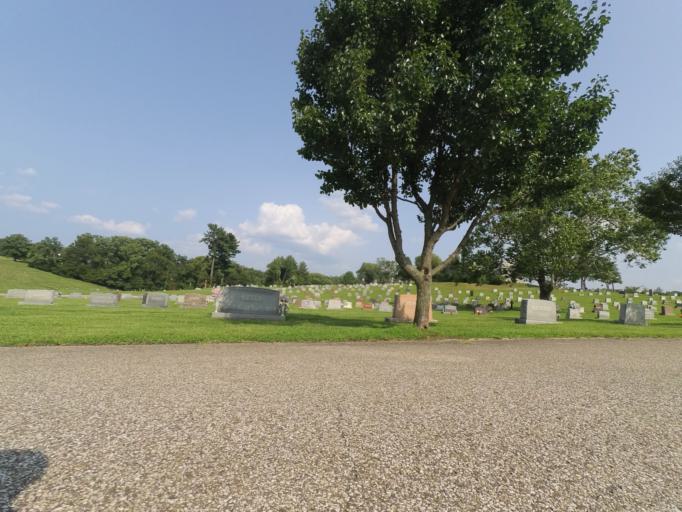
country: US
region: West Virginia
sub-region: Cabell County
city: Huntington
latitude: 38.4053
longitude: -82.3992
